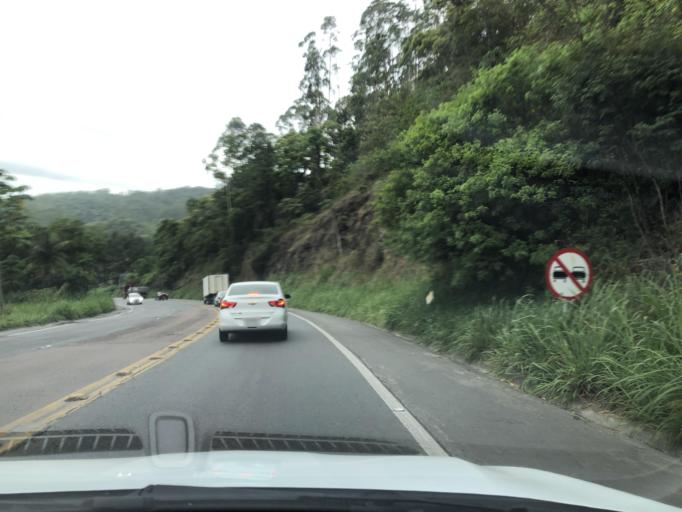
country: BR
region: Santa Catarina
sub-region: Ibirama
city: Ibirama
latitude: -27.0882
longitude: -49.5191
